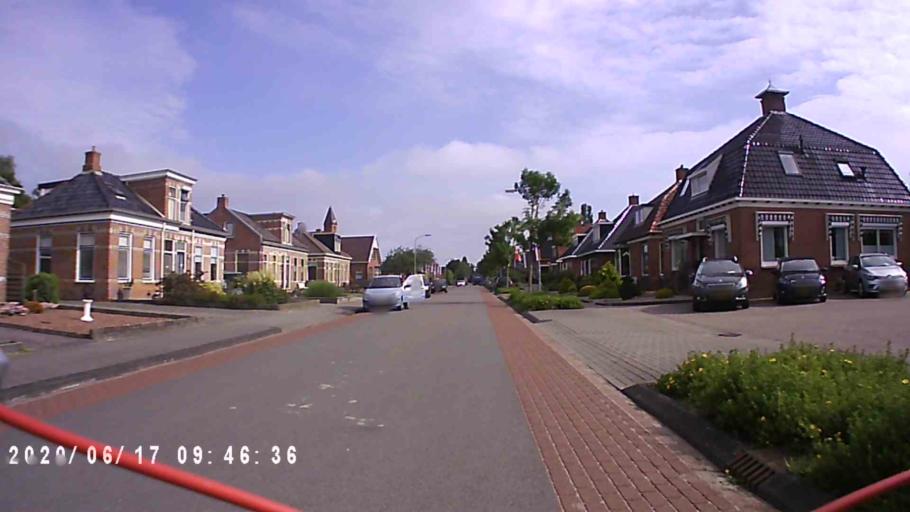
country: NL
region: Groningen
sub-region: Gemeente De Marne
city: Ulrum
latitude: 53.3559
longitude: 6.3380
